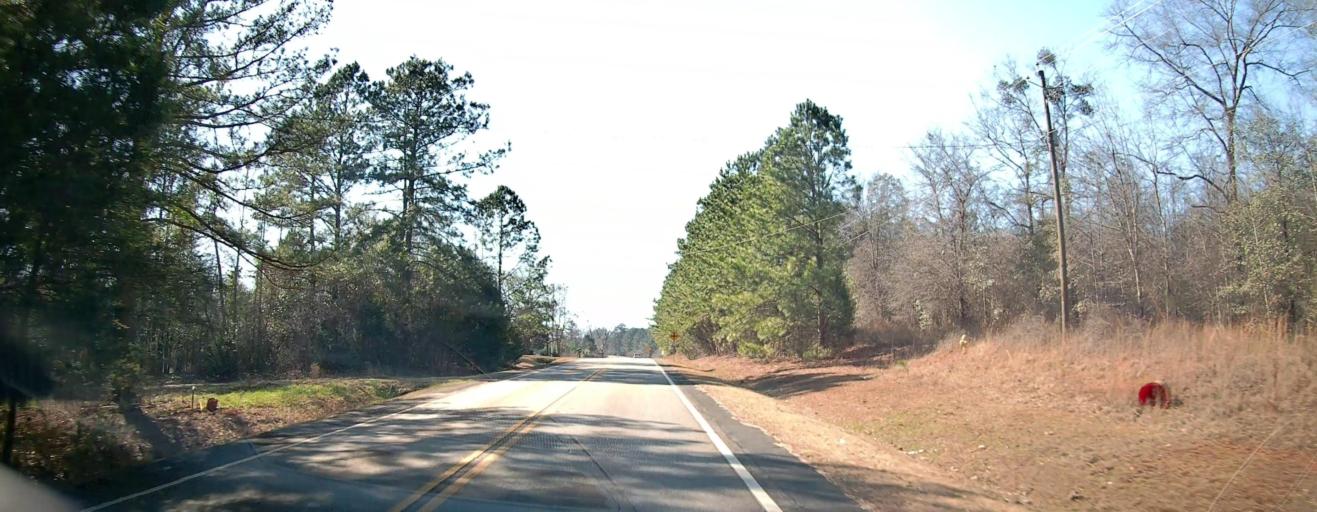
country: US
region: Georgia
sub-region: Macon County
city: Oglethorpe
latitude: 32.1965
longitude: -84.1503
